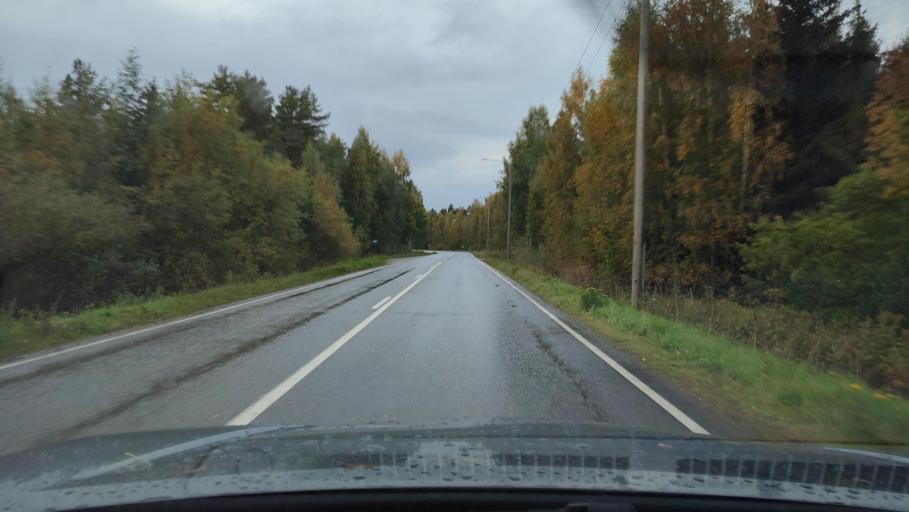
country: FI
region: Southern Ostrobothnia
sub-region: Suupohja
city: Karijoki
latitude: 62.2395
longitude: 21.6034
